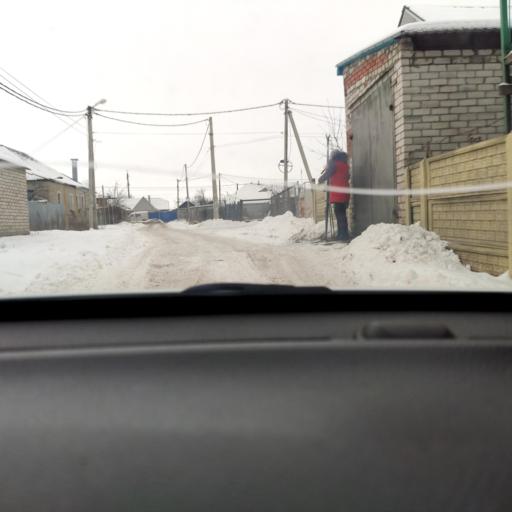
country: RU
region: Voronezj
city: Volya
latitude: 51.7512
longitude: 39.4982
